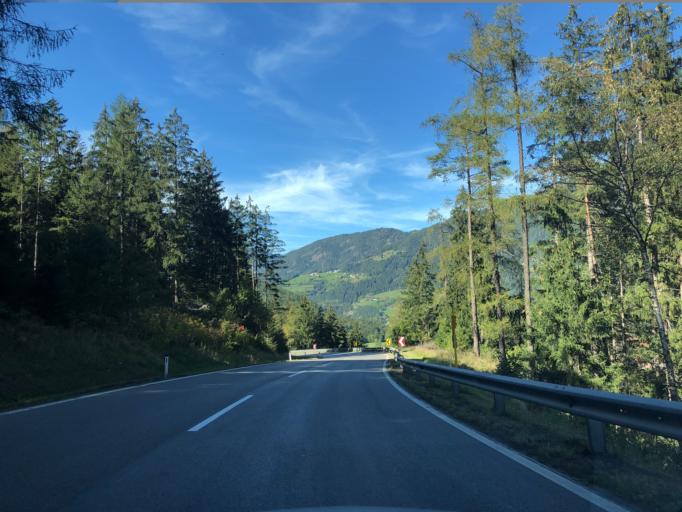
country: AT
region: Tyrol
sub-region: Politischer Bezirk Imst
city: Oetz
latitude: 47.1826
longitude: 10.9096
